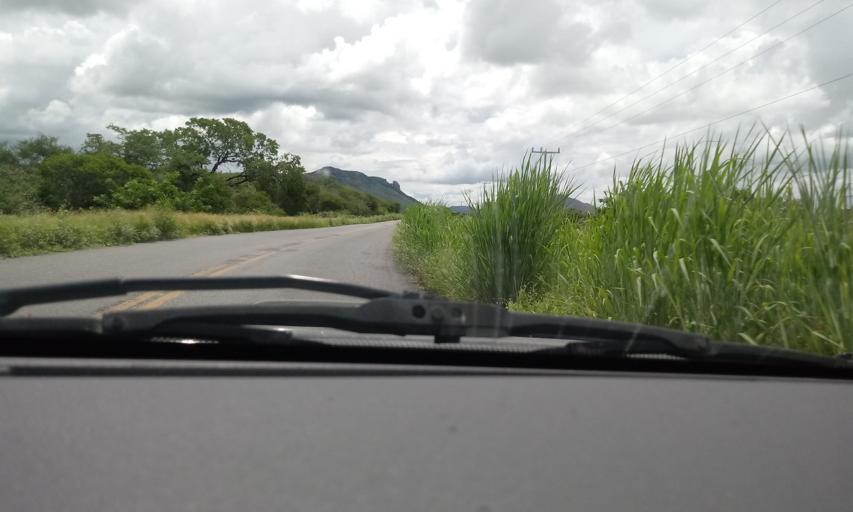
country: BR
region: Bahia
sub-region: Guanambi
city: Guanambi
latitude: -14.1651
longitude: -42.8155
